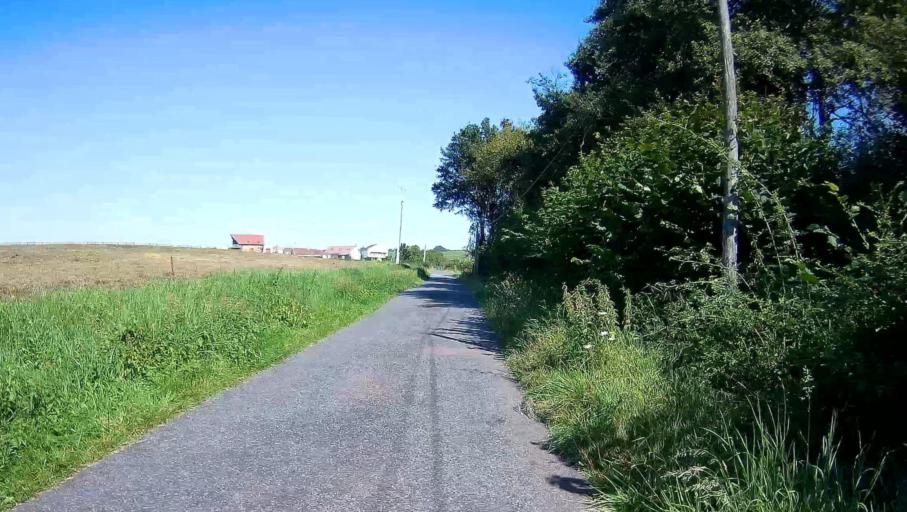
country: FR
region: Bourgogne
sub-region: Departement de Saone-et-Loire
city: Couches
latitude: 46.8393
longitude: 4.5824
